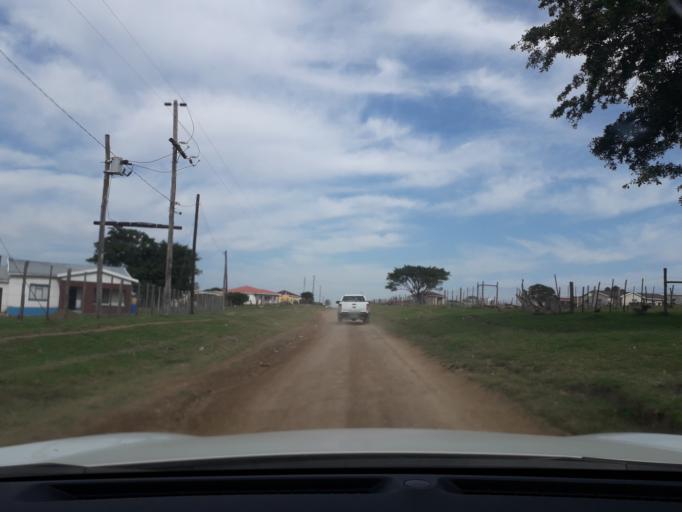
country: ZA
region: Eastern Cape
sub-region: Buffalo City Metropolitan Municipality
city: Bhisho
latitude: -32.9872
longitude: 27.3606
